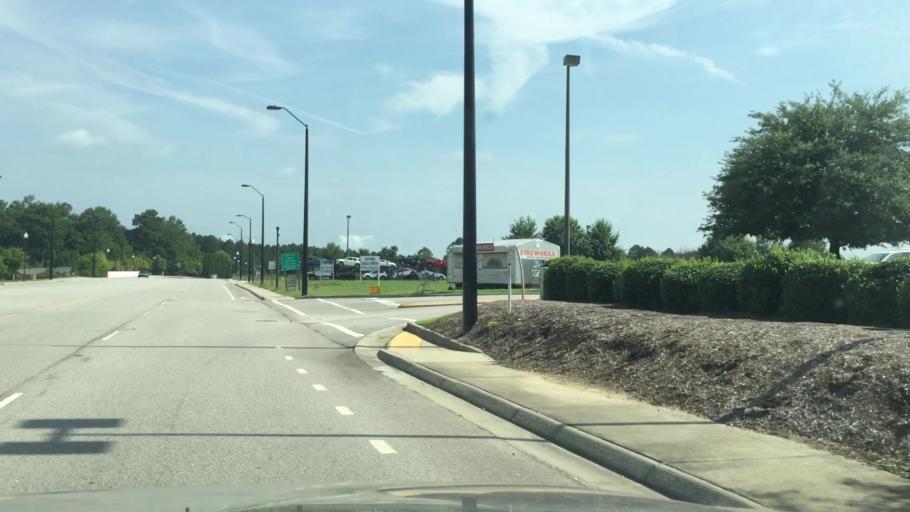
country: US
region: South Carolina
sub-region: Sumter County
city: Sumter
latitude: 33.9580
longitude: -80.3878
